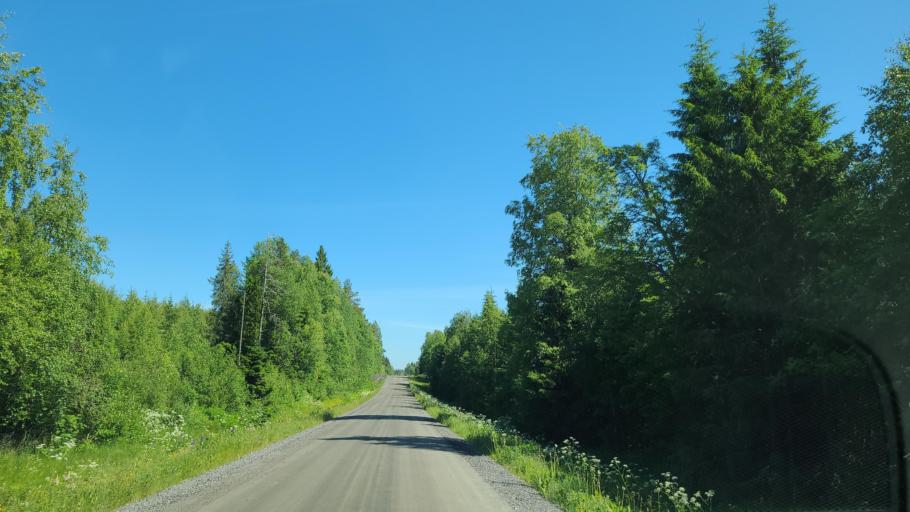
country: SE
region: Vaesterbotten
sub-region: Bjurholms Kommun
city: Bjurholm
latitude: 63.6422
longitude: 19.1275
